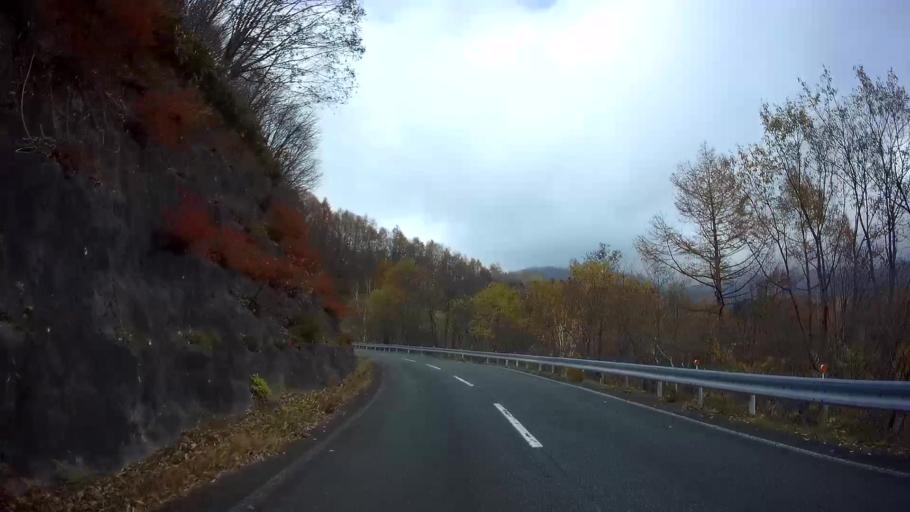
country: JP
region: Gunma
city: Nakanojomachi
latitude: 36.6797
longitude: 138.6633
